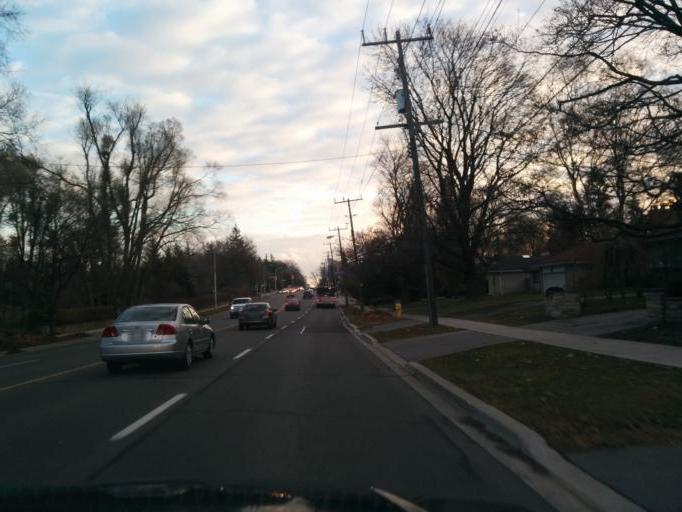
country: CA
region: Ontario
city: Etobicoke
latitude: 43.6701
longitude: -79.5347
